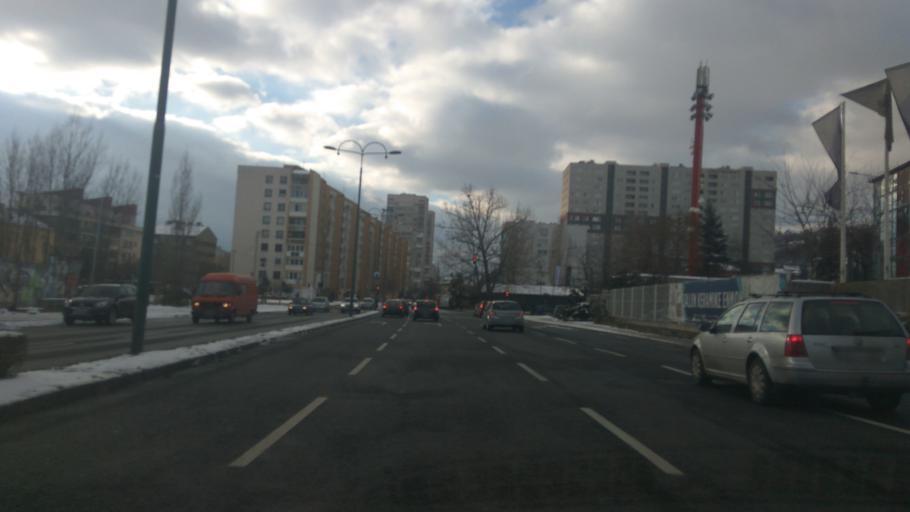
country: BA
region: Federation of Bosnia and Herzegovina
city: Kobilja Glava
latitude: 43.8566
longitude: 18.3856
